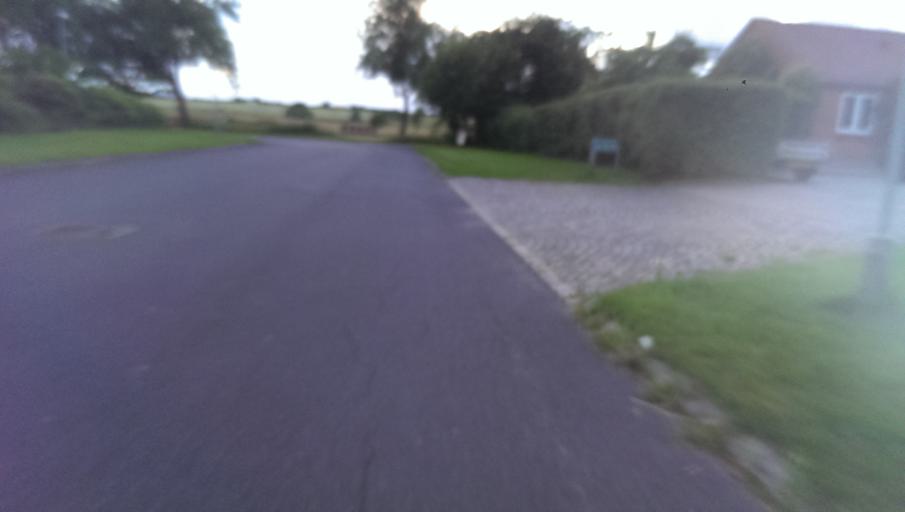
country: DK
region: South Denmark
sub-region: Esbjerg Kommune
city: Tjaereborg
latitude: 55.4732
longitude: 8.5693
